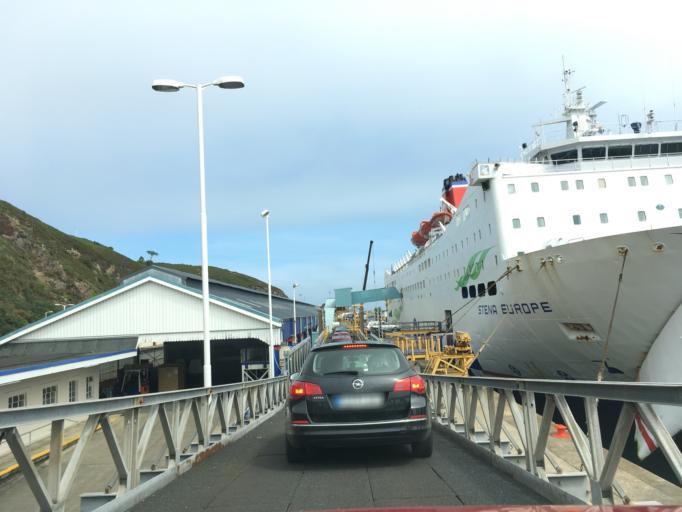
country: GB
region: Wales
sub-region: Pembrokeshire
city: Goodwick
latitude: 52.0097
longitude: -4.9864
